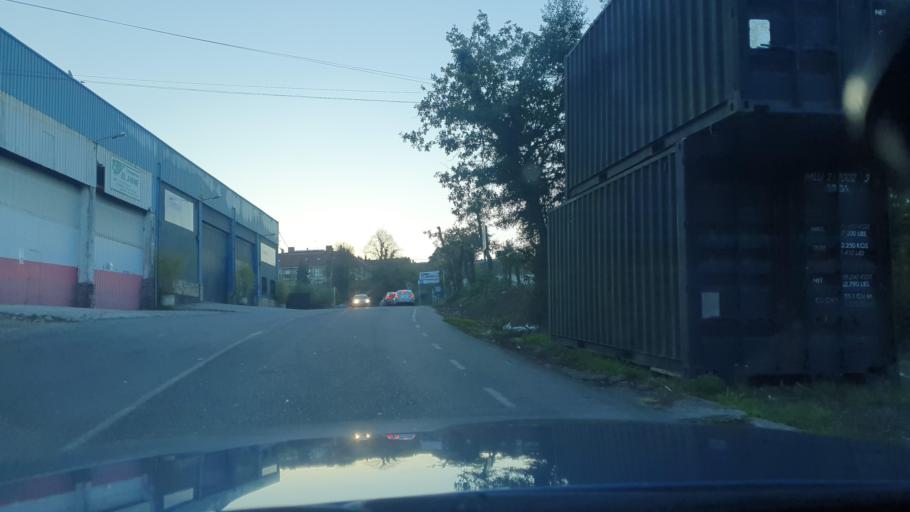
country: ES
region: Galicia
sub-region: Provincia da Coruna
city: Santiago de Compostela
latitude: 42.8436
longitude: -8.5829
